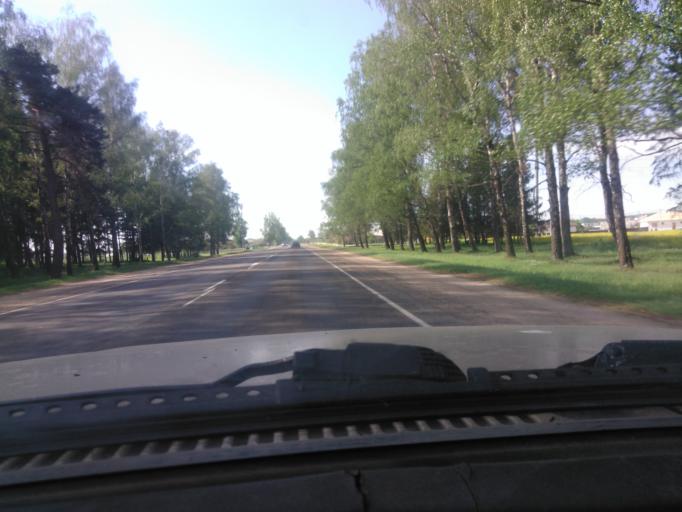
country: BY
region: Mogilev
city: Buynichy
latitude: 53.8421
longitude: 30.2491
